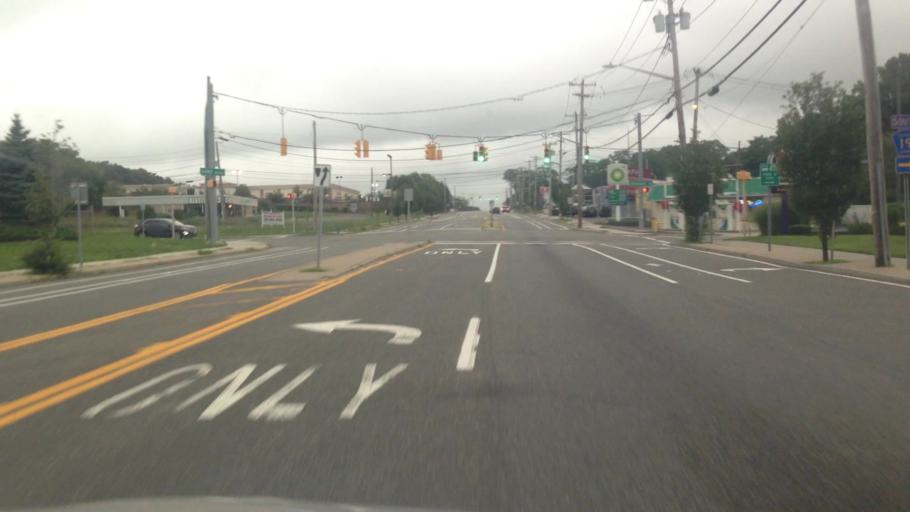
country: US
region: New York
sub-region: Suffolk County
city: Ronkonkoma
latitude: 40.8283
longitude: -73.0987
